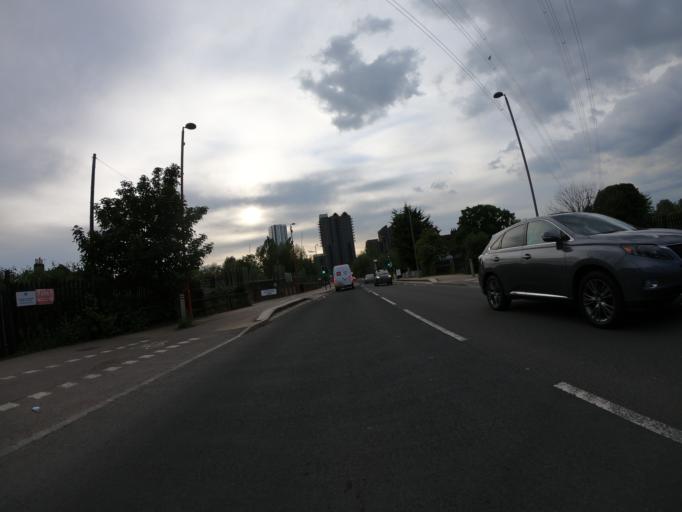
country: GB
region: England
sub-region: Greater London
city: Walthamstow
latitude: 51.5863
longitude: -0.0519
